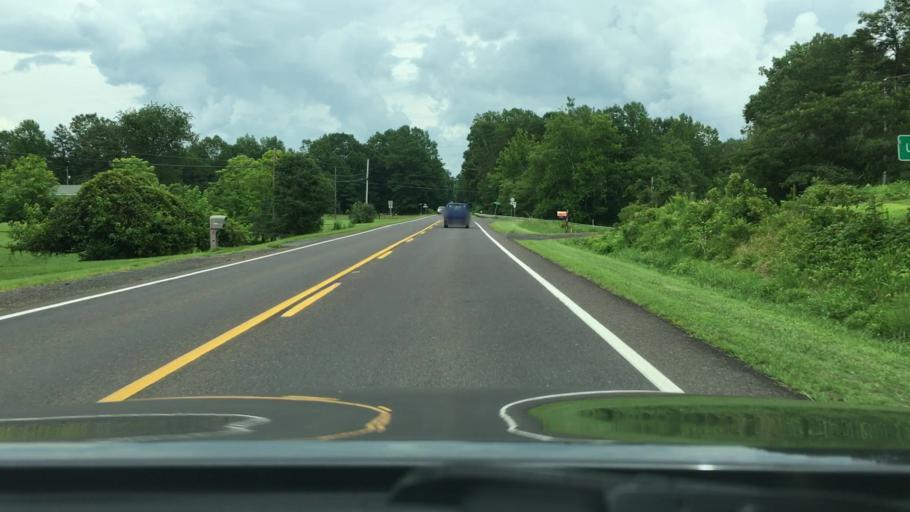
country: US
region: Virginia
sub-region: Orange County
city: Orange
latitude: 38.2617
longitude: -77.9859
